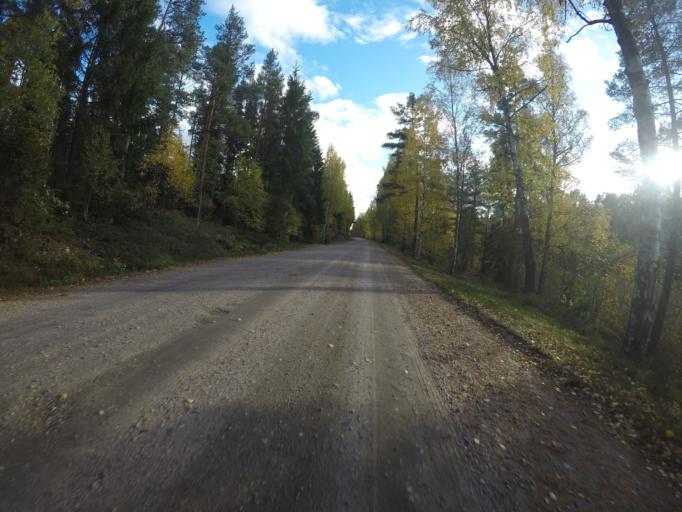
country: SE
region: Vaestmanland
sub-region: Arboga Kommun
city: Tyringe
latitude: 59.3418
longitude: 15.9622
